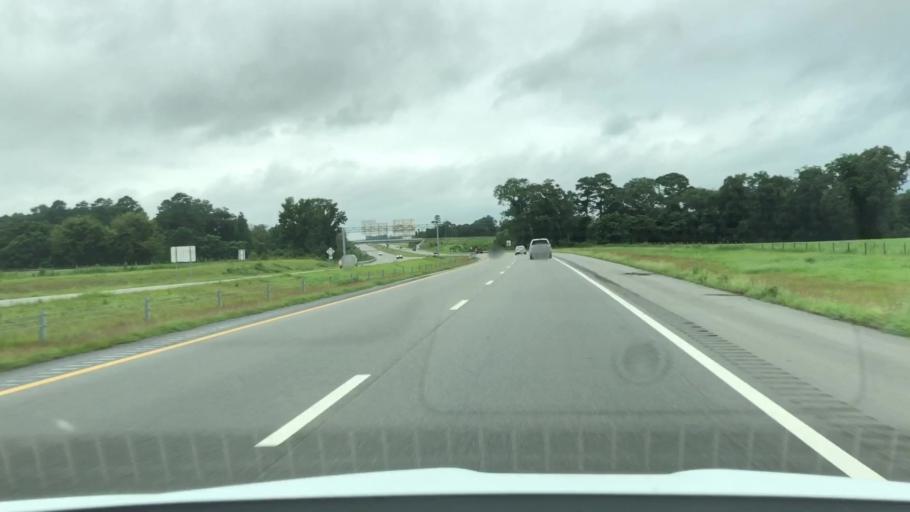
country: US
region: North Carolina
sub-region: Lenoir County
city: La Grange
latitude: 35.3070
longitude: -77.8208
